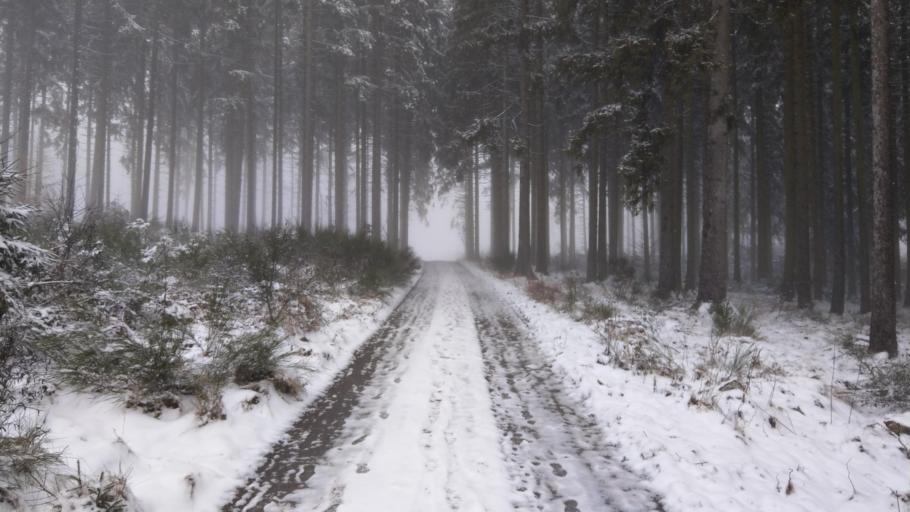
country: DE
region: North Rhine-Westphalia
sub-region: Regierungsbezirk Arnsberg
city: Erndtebruck
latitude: 50.9853
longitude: 8.2160
